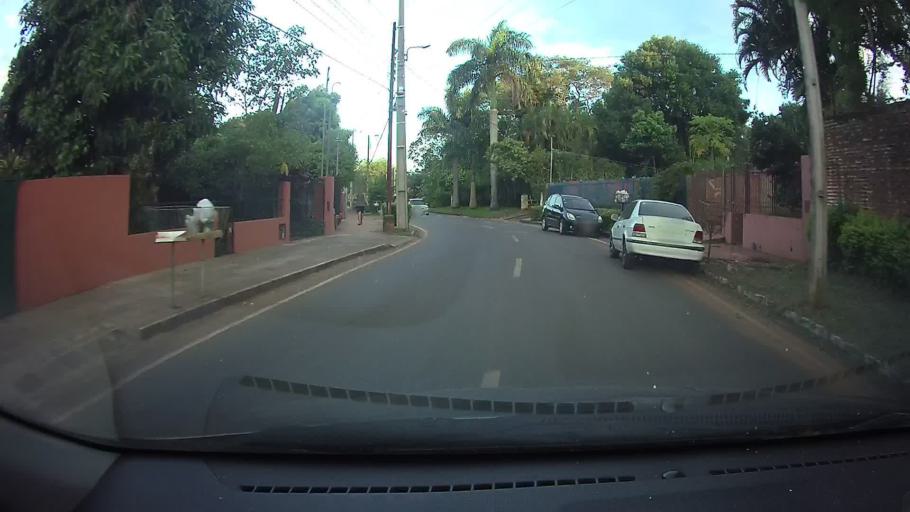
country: PY
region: Central
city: San Lorenzo
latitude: -25.2623
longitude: -57.4925
